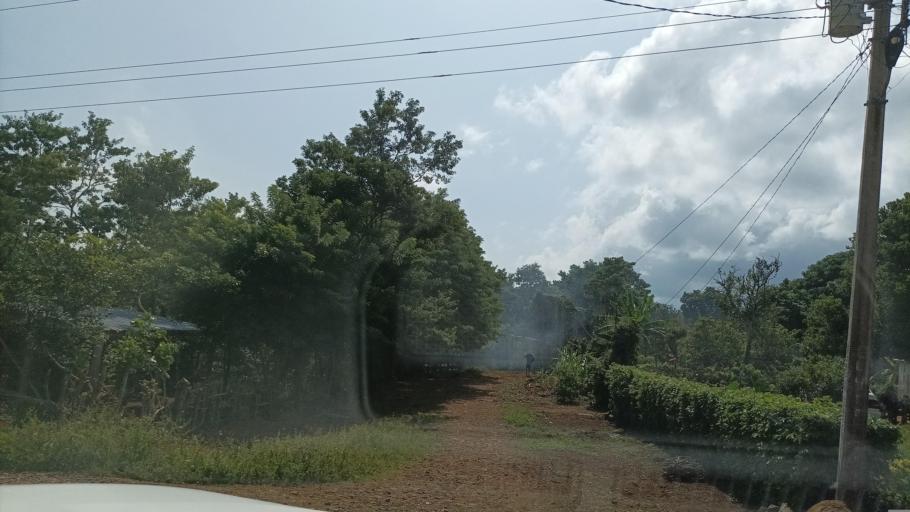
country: MX
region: Veracruz
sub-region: Pajapan
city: Pajapan
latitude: 18.2661
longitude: -94.6829
